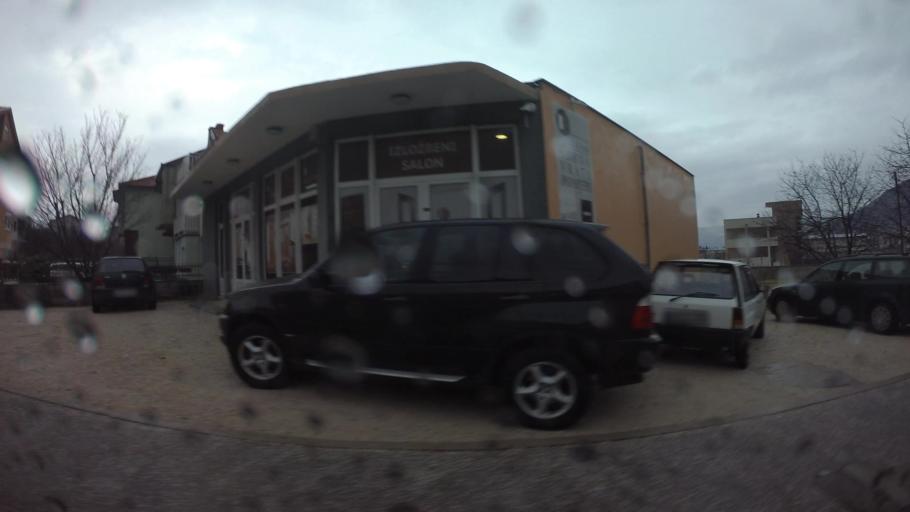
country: BA
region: Federation of Bosnia and Herzegovina
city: Rodoc
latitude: 43.3184
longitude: 17.8345
